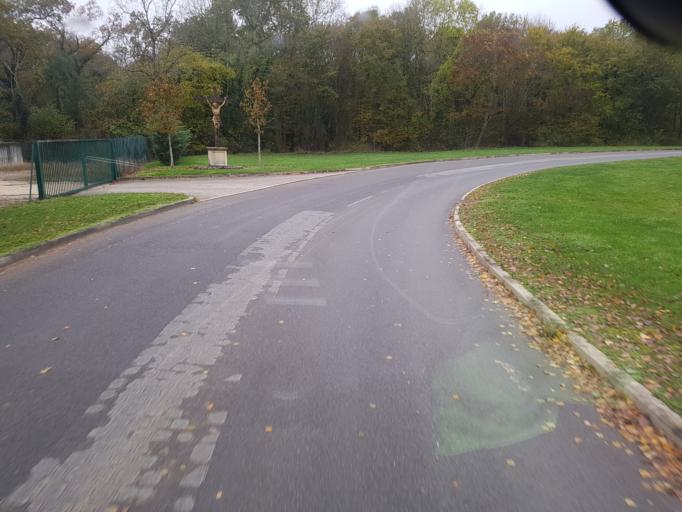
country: FR
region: Bourgogne
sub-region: Departement de la Cote-d'Or
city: Arc-sur-Tille
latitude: 47.3177
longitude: 5.2027
